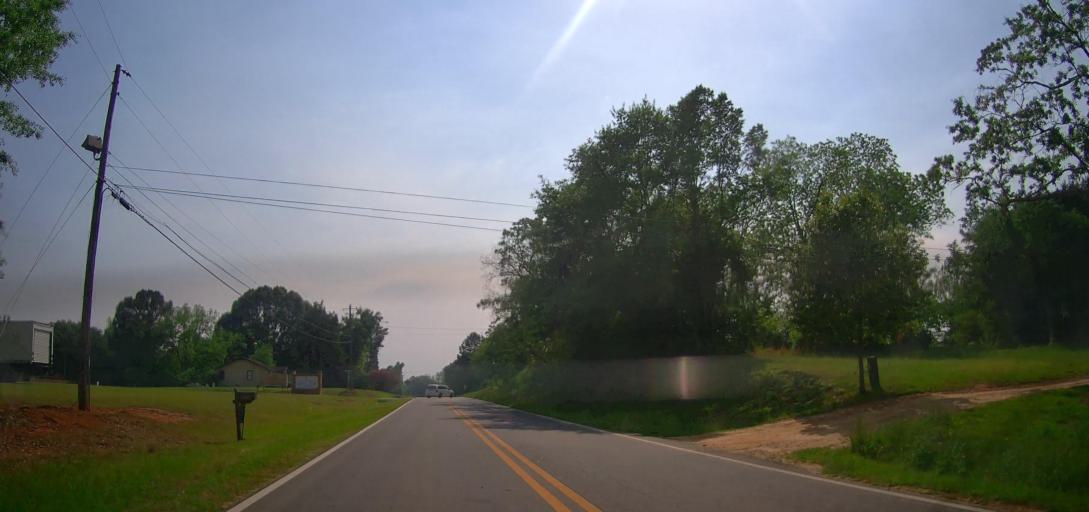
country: US
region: Georgia
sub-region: Laurens County
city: East Dublin
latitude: 32.5636
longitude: -82.8666
